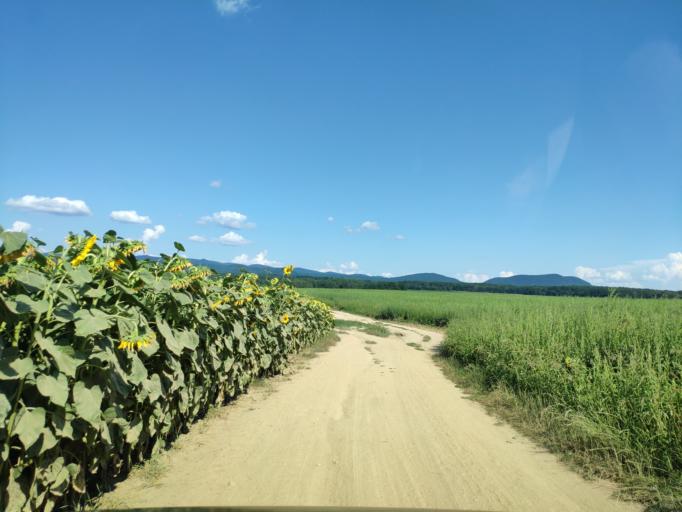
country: SK
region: Presovsky
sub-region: Okres Presov
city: Presov
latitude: 48.9078
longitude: 21.2661
